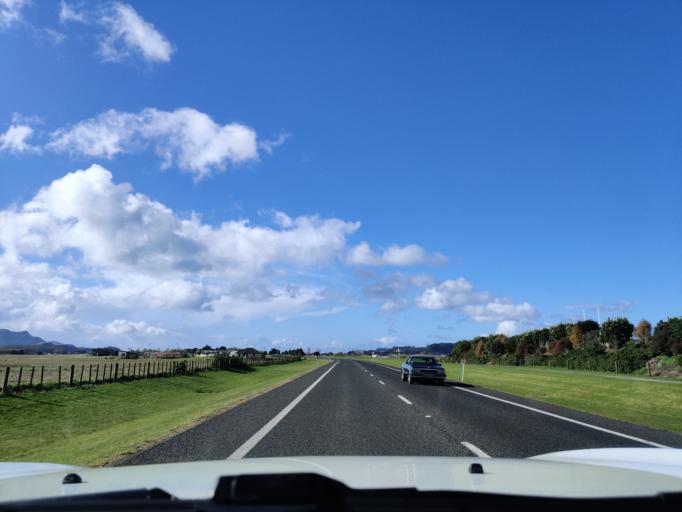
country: NZ
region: Waikato
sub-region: Thames-Coromandel District
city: Whitianga
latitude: -36.8325
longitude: 175.6784
